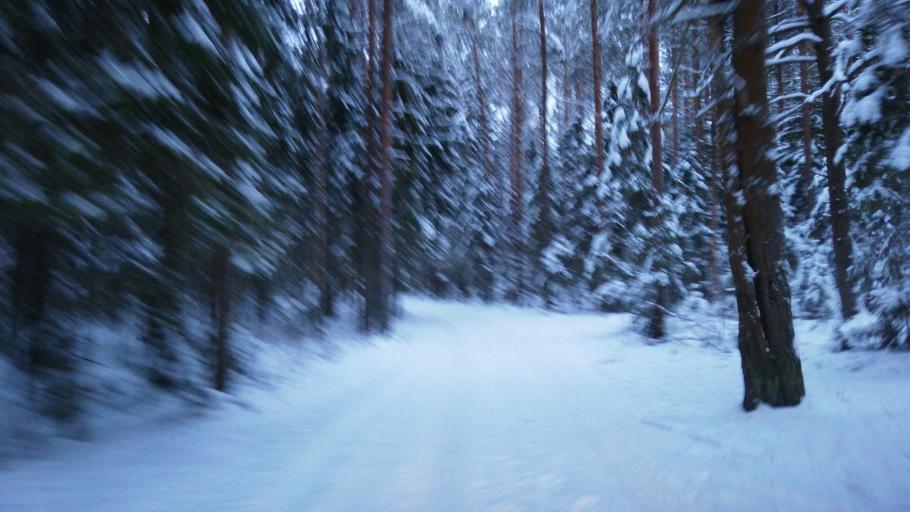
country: RU
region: Jaroslavl
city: Krasnyye Tkachi
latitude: 57.4472
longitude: 39.7976
